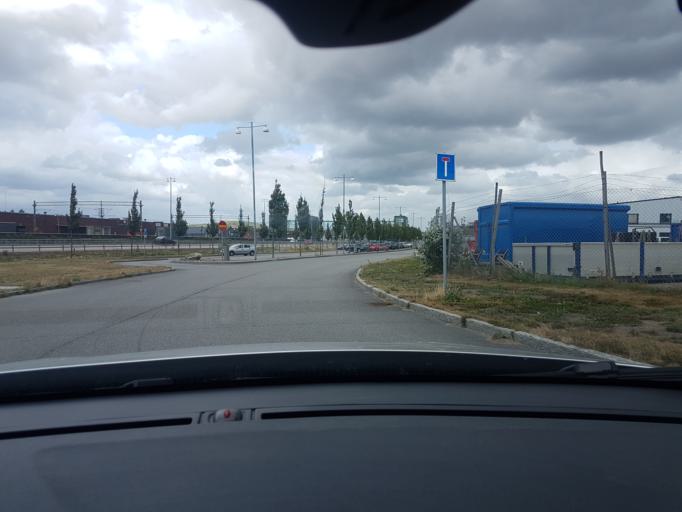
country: SE
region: Vaestra Goetaland
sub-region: Ale Kommun
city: Alvangen
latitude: 57.9564
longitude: 12.1139
